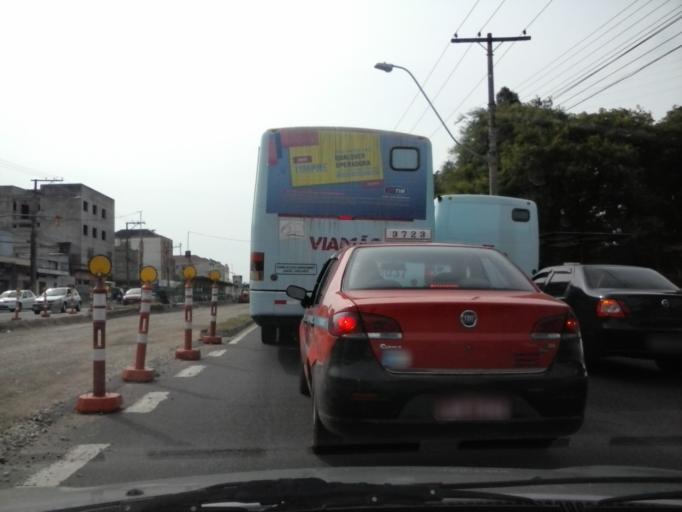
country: BR
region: Rio Grande do Sul
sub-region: Porto Alegre
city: Porto Alegre
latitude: -30.0623
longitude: -51.1875
